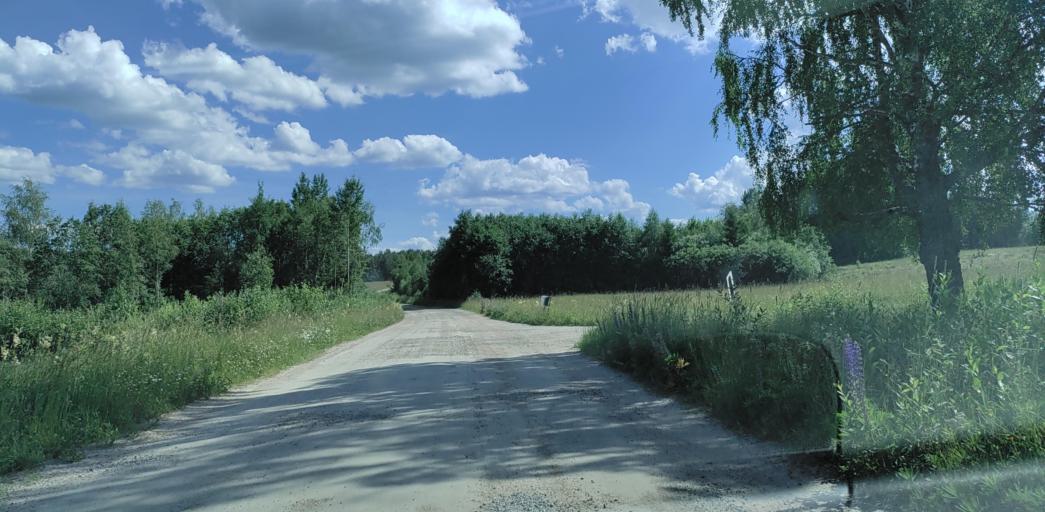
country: SE
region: Vaermland
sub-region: Hagfors Kommun
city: Ekshaerad
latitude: 60.1256
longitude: 13.4780
